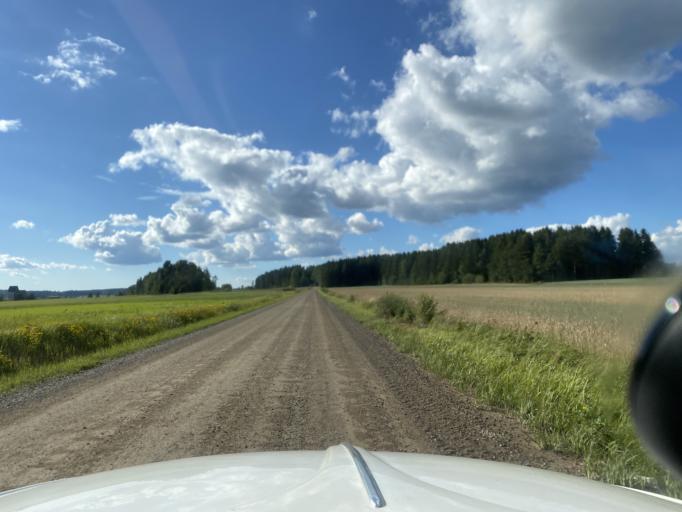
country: FI
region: Pirkanmaa
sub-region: Lounais-Pirkanmaa
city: Punkalaidun
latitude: 61.1358
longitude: 23.2241
